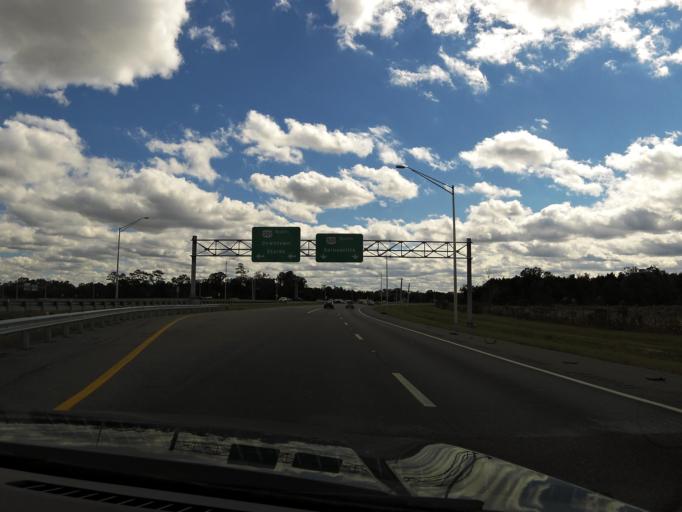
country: US
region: Florida
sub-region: Bradford County
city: Starke
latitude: 29.9183
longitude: -82.1355
